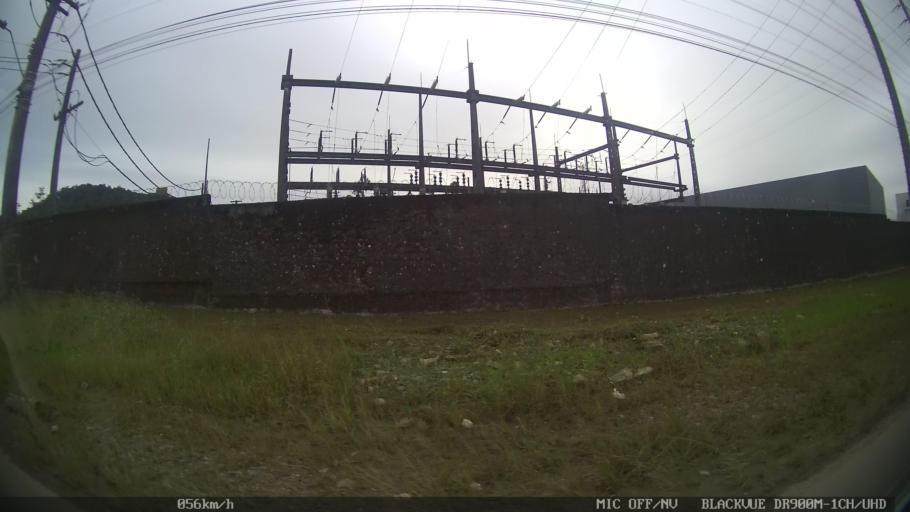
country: BR
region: Santa Catarina
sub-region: Joinville
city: Joinville
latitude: -26.2314
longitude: -48.9092
